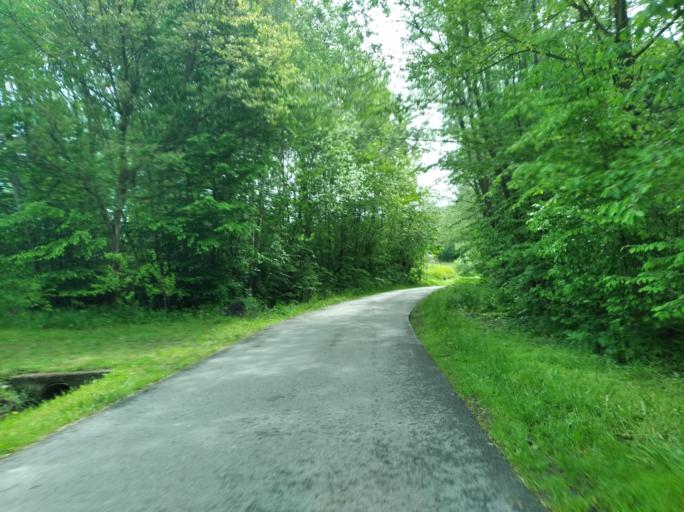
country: PL
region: Subcarpathian Voivodeship
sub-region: Powiat strzyzowski
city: Strzyzow
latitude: 49.9305
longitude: 21.7344
